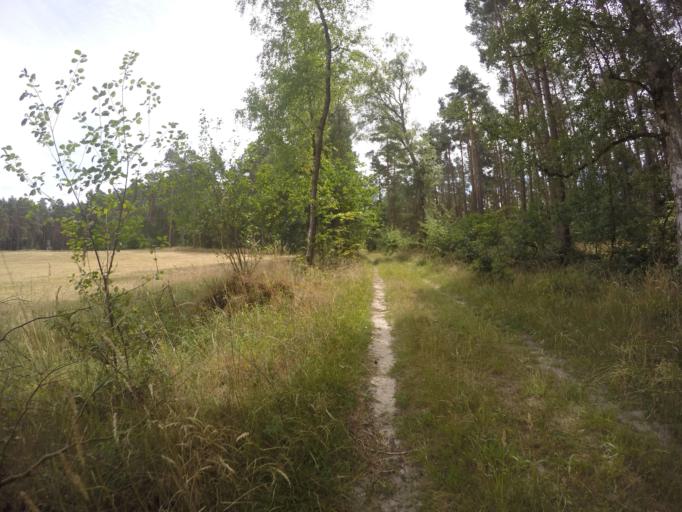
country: DE
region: Lower Saxony
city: Thomasburg
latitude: 53.2500
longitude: 10.6682
